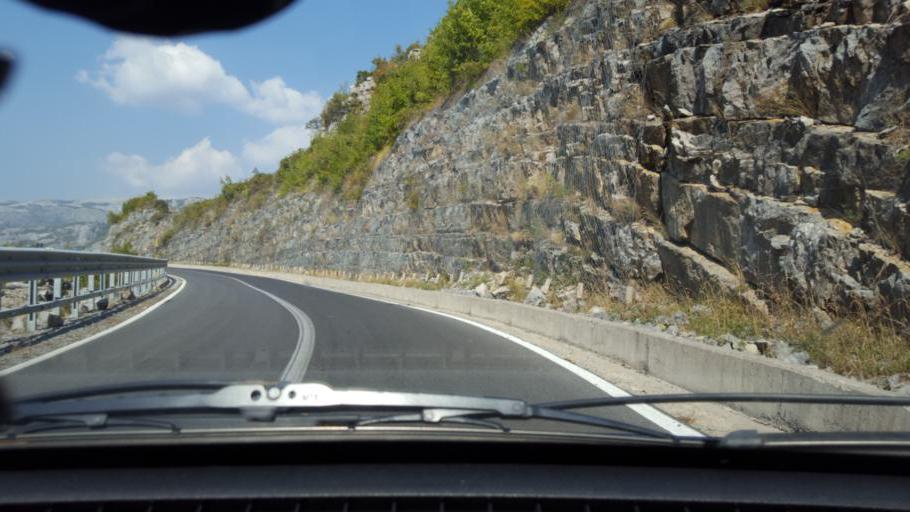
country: AL
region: Shkoder
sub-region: Rrethi i Malesia e Madhe
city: Kastrat
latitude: 42.4138
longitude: 19.5038
